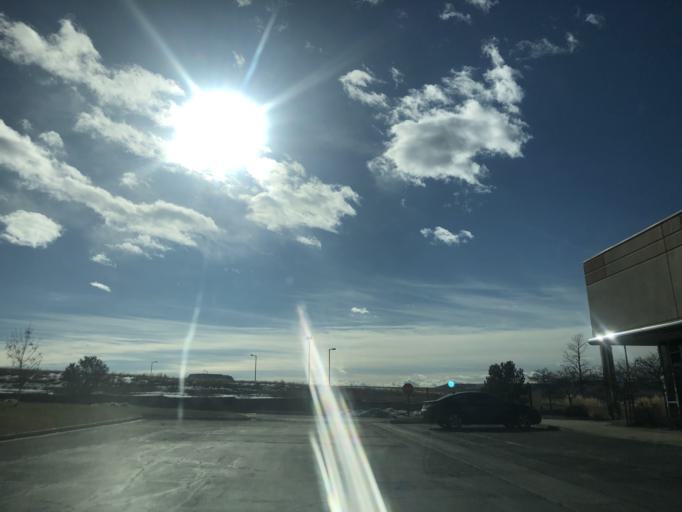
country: US
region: Colorado
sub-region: Douglas County
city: Meridian
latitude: 39.5588
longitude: -104.8577
